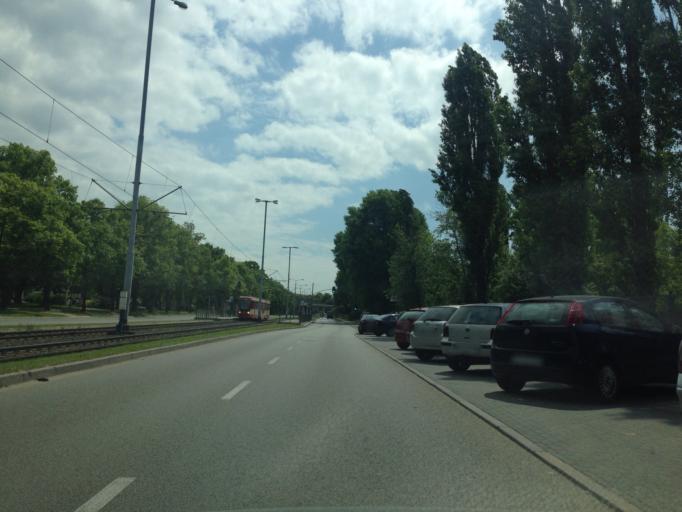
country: PL
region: Pomeranian Voivodeship
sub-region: Gdansk
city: Gdansk
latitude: 54.3799
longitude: 18.6219
